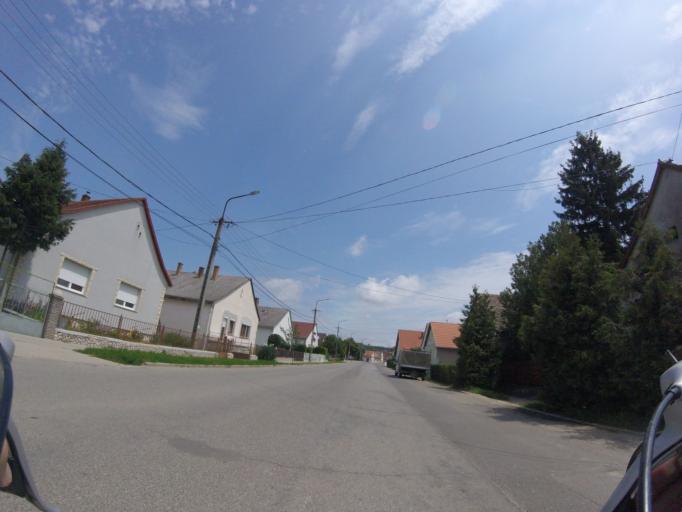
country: HU
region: Baranya
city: Boly
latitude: 45.9968
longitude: 18.4486
